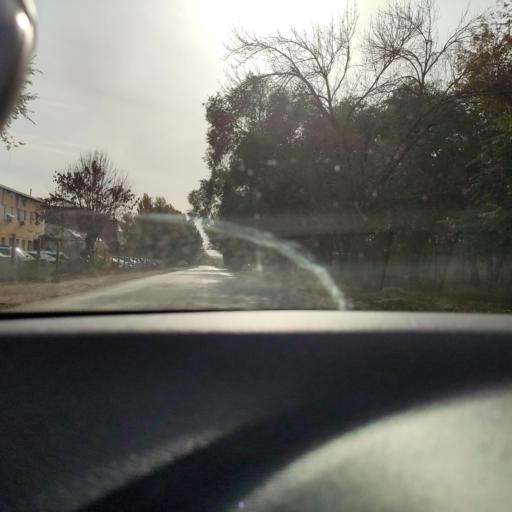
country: RU
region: Samara
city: Samara
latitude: 53.1866
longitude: 50.2447
